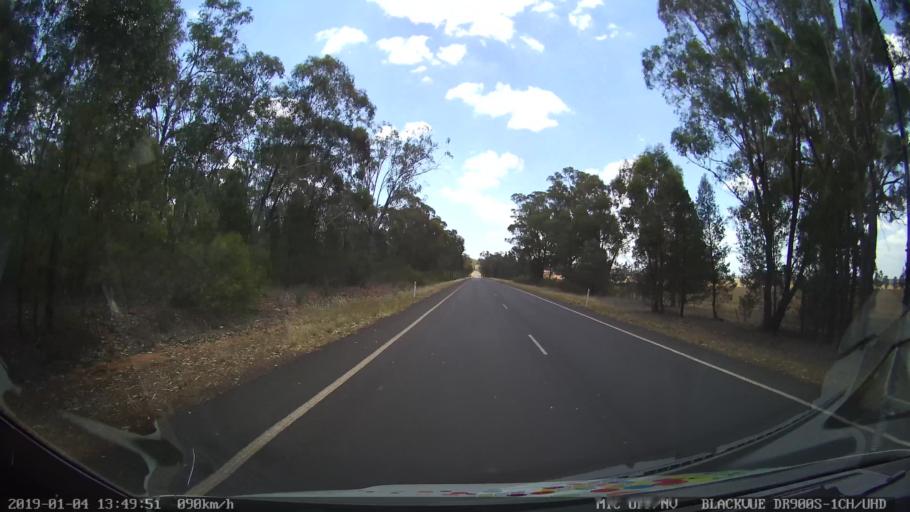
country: AU
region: New South Wales
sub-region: Dubbo Municipality
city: Dubbo
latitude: -32.4270
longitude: 148.5766
